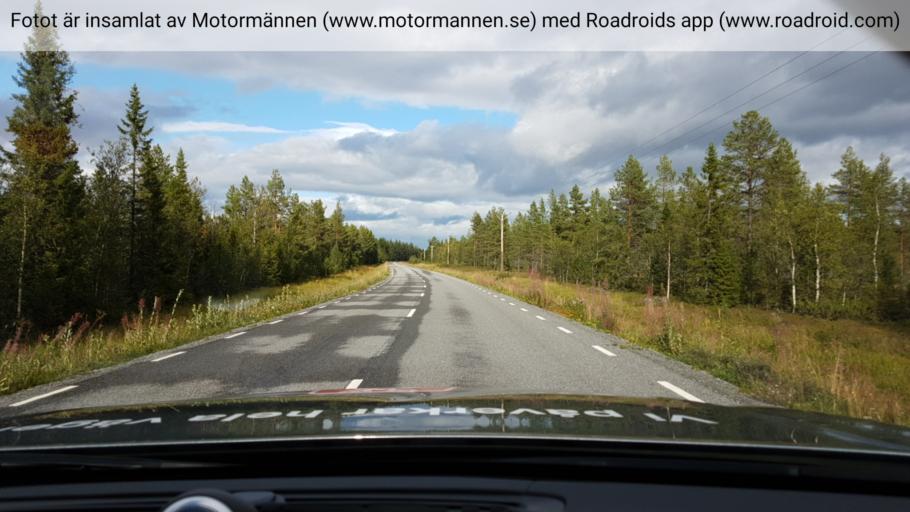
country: SE
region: Jaemtland
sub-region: Krokoms Kommun
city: Krokom
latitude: 63.6506
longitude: 14.4603
